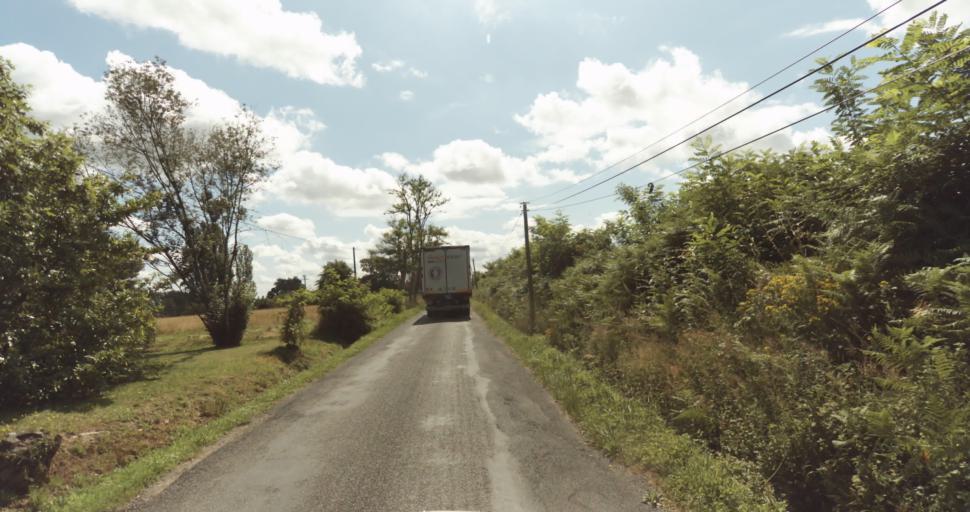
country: FR
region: Aquitaine
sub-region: Departement de la Gironde
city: Bazas
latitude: 44.4520
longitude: -0.2142
